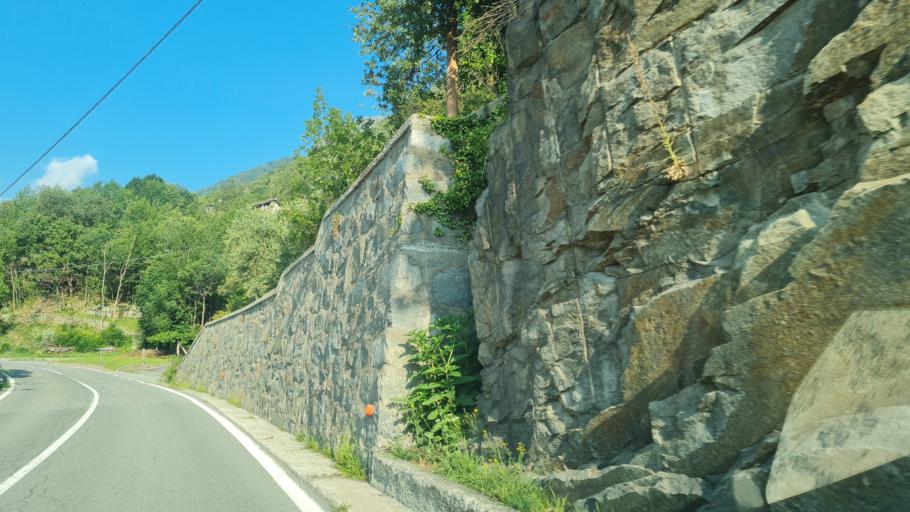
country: IT
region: Aosta Valley
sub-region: Valle d'Aosta
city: Hone
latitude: 45.6137
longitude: 7.7261
